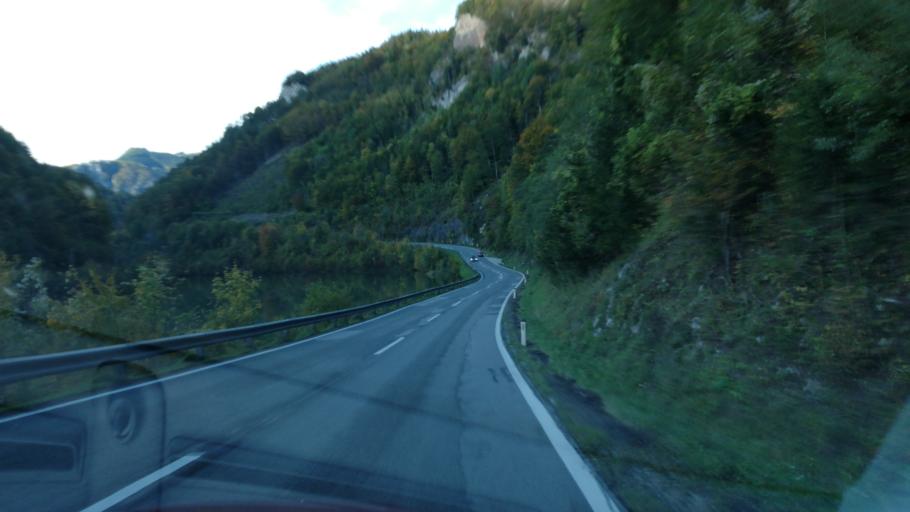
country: AT
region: Upper Austria
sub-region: Politischer Bezirk Steyr-Land
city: Weyer
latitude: 47.8341
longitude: 14.6446
